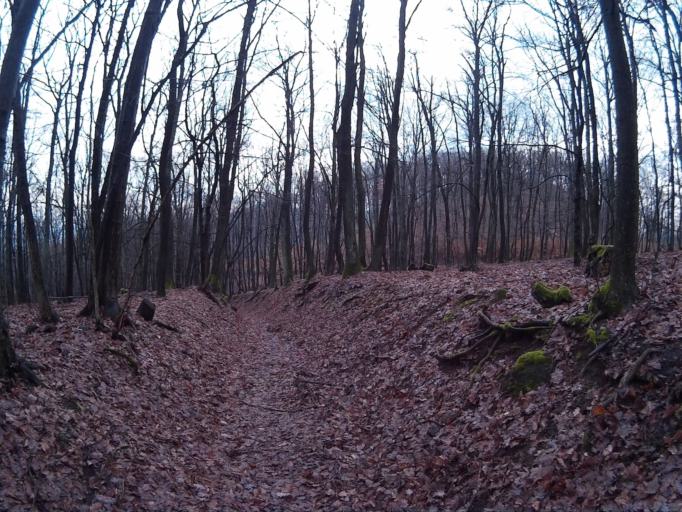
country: HU
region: Borsod-Abauj-Zemplen
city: Satoraljaujhely
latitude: 48.4162
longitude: 21.5903
